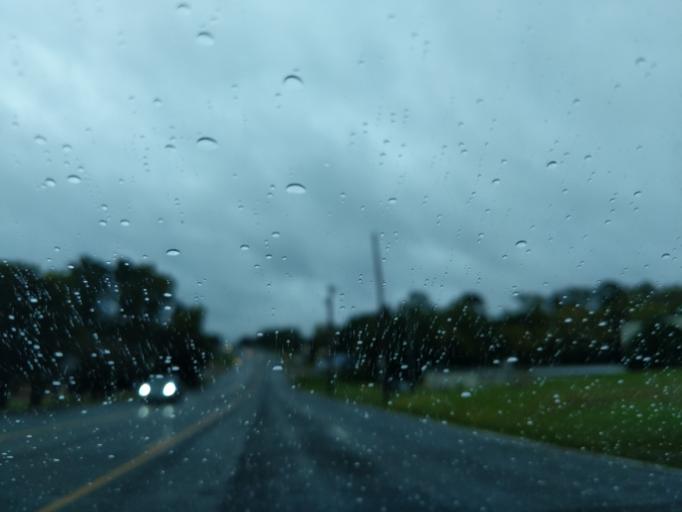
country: US
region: Texas
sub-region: Nacogdoches County
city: Nacogdoches
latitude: 31.5828
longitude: -94.6690
